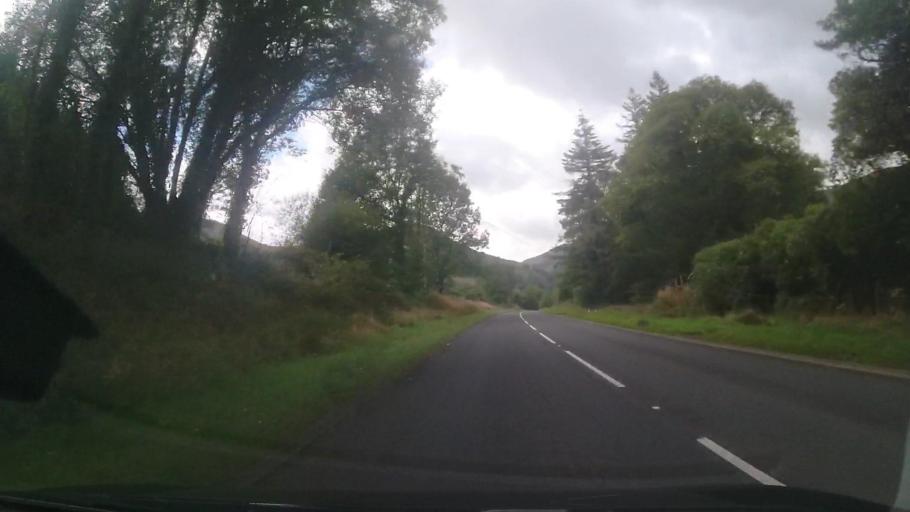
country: GB
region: Wales
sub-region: Gwynedd
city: Corris
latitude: 52.7238
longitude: -3.7043
